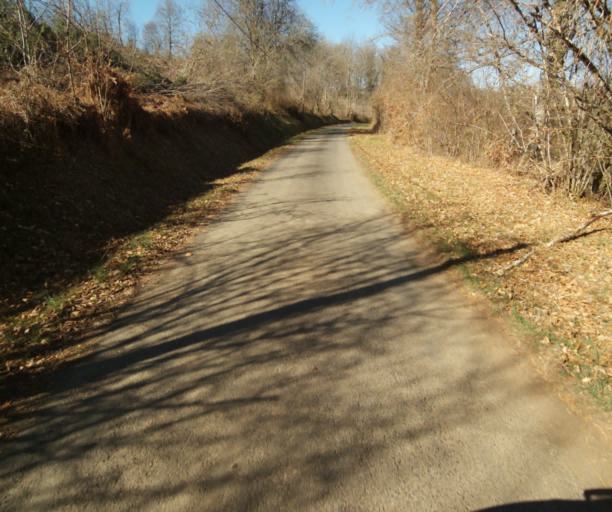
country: FR
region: Limousin
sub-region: Departement de la Correze
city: Chamboulive
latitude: 45.4174
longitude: 1.7170
